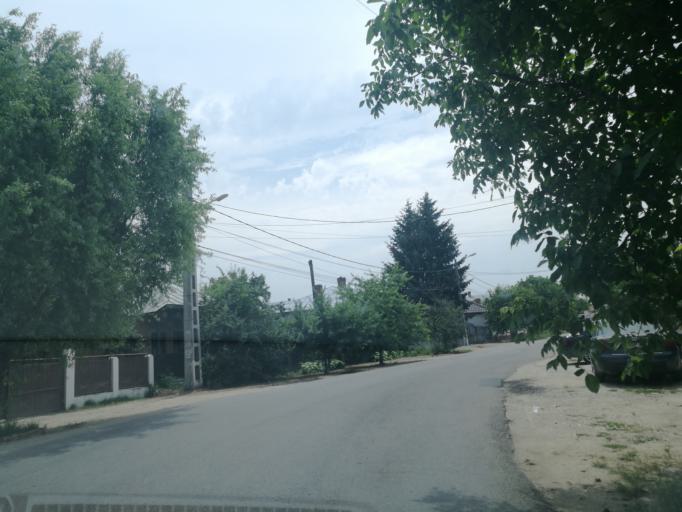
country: RO
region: Ilfov
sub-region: Comuna Vidra
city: Vidra
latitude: 44.2662
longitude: 26.1531
